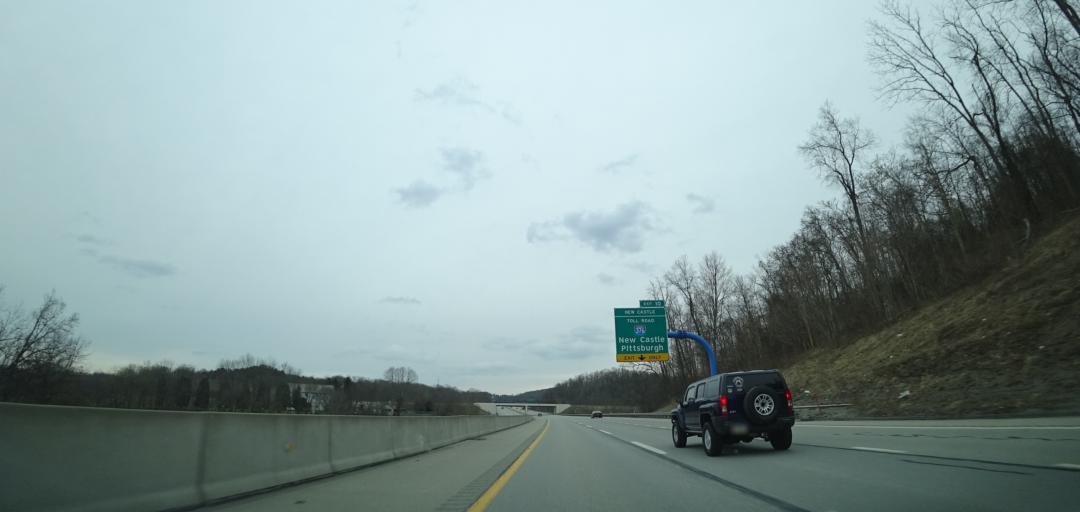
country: US
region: Pennsylvania
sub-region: Beaver County
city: Big Beaver
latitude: 40.8437
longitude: -80.3896
